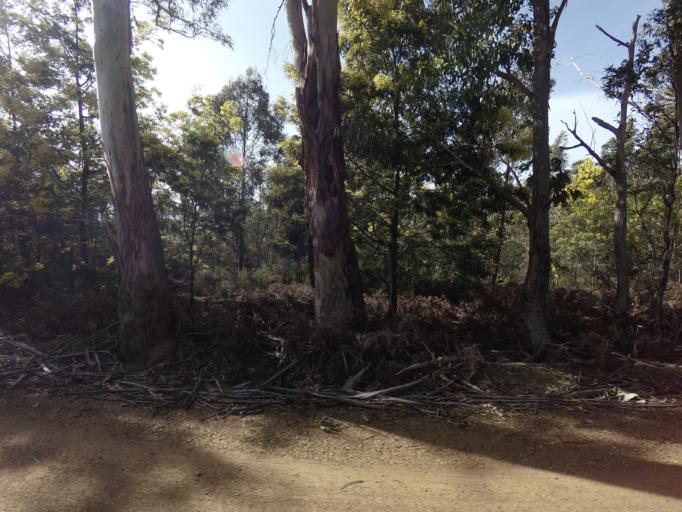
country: AU
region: Tasmania
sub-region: Kingborough
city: Kettering
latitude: -43.0903
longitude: 147.2659
